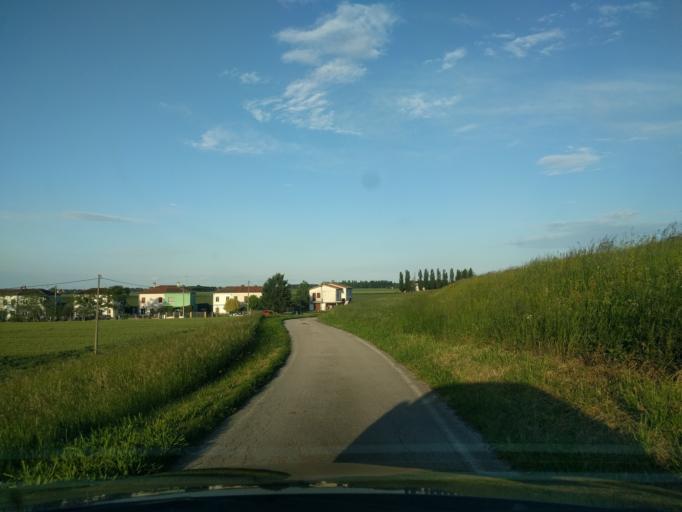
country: IT
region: Veneto
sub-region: Provincia di Rovigo
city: Guarda Veneta
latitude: 44.9798
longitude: 11.8151
